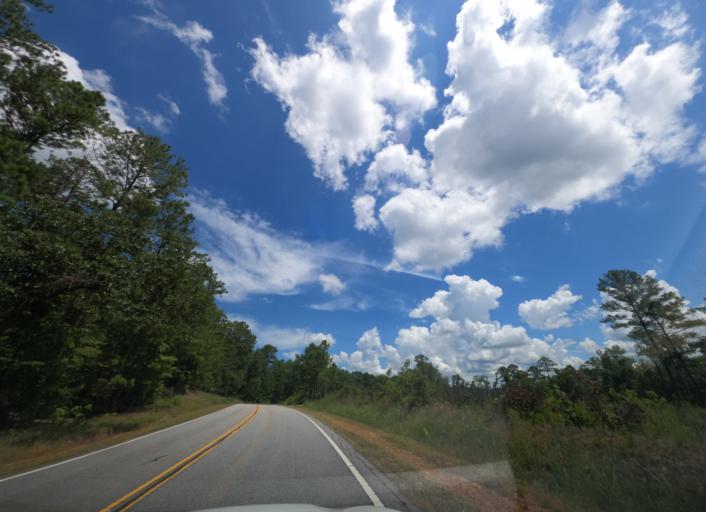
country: US
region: Georgia
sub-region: Lincoln County
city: Lincolnton
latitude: 33.8836
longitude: -82.4095
